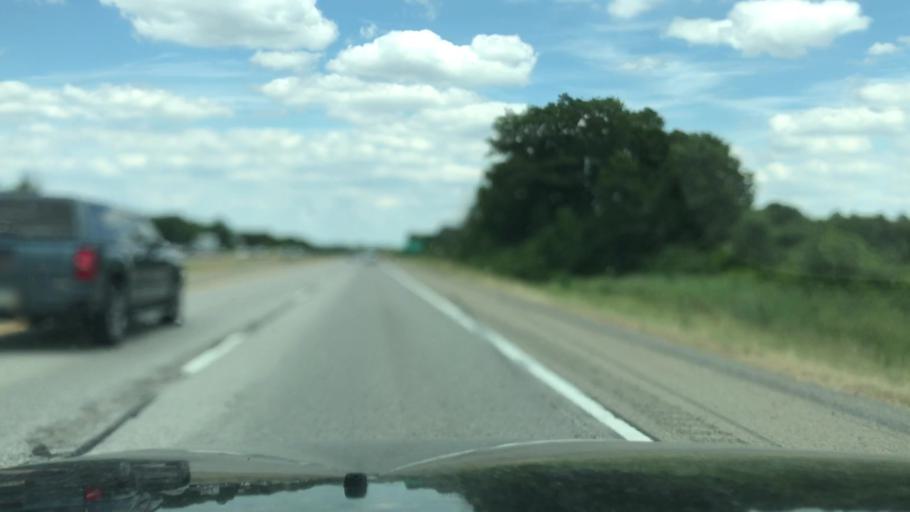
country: US
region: Michigan
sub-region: Ottawa County
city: Hudsonville
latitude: 42.8535
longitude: -85.8462
